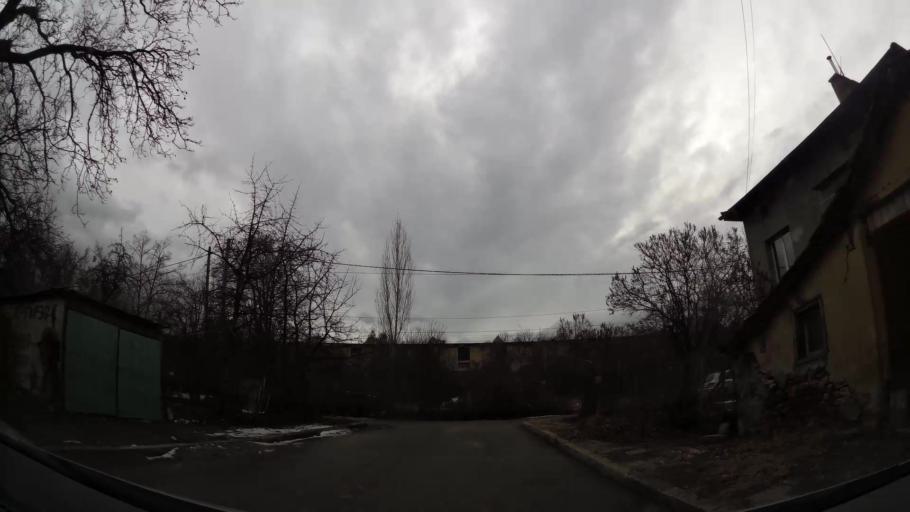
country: BG
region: Sofia-Capital
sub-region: Stolichna Obshtina
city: Sofia
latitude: 42.7218
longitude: 23.3006
